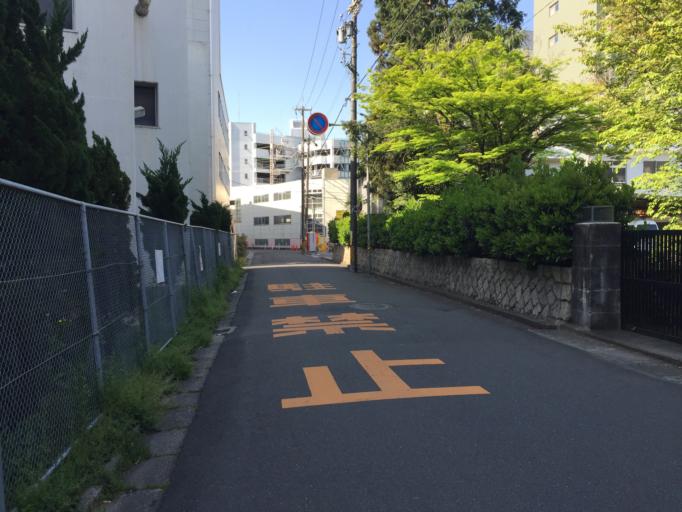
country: JP
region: Mie
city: Yokkaichi
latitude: 34.9689
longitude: 136.6186
